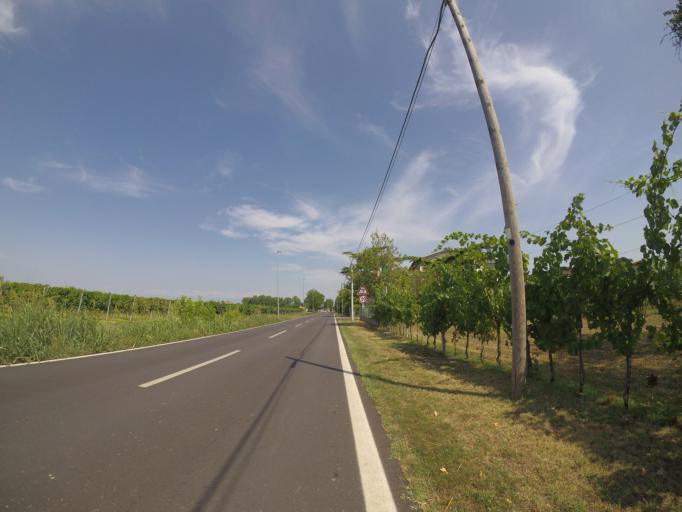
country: IT
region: Friuli Venezia Giulia
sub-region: Provincia di Pordenone
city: Ramuscello
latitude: 45.9075
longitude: 12.8917
